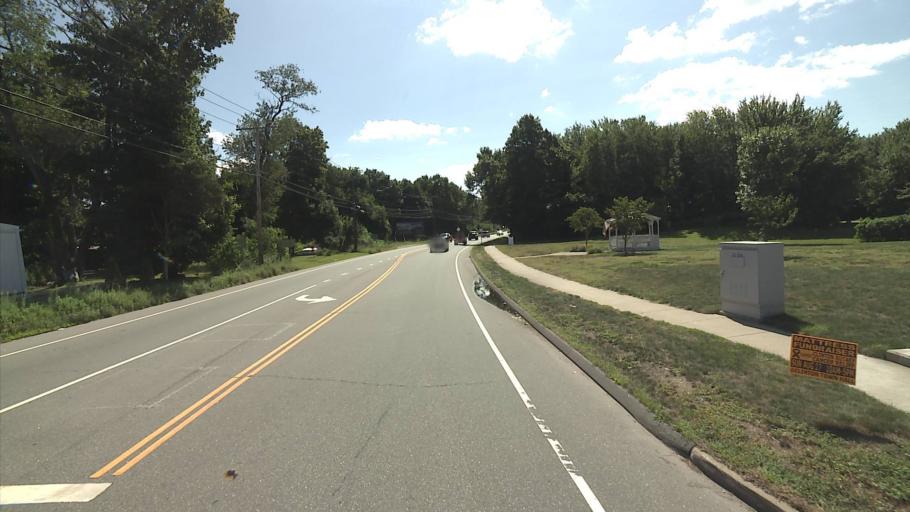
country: US
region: Connecticut
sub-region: Middlesex County
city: Clinton
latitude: 41.2758
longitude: -72.5121
